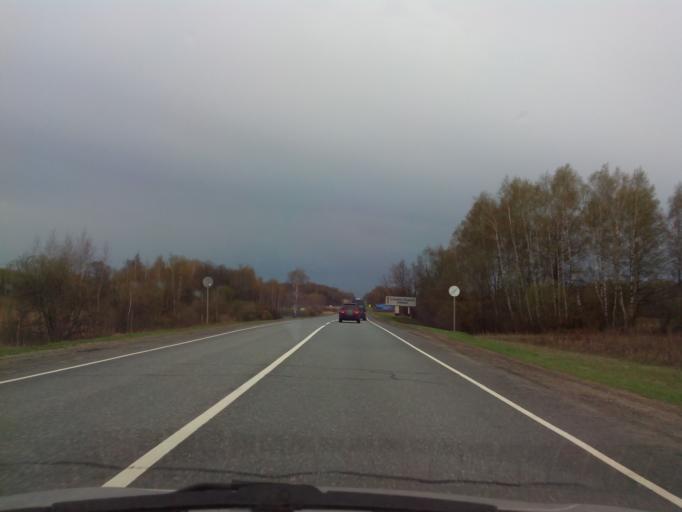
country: RU
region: Moskovskaya
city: Uzunovo
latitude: 54.5709
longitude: 38.4531
